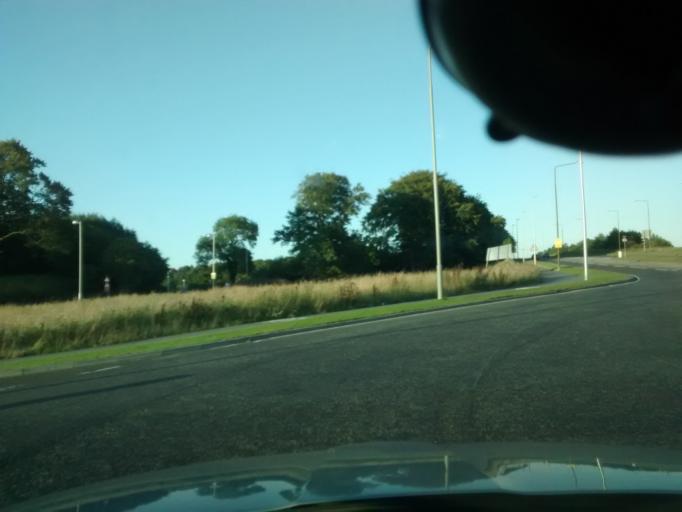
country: GB
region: Scotland
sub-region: West Lothian
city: Blackburn
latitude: 55.8916
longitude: -3.6143
